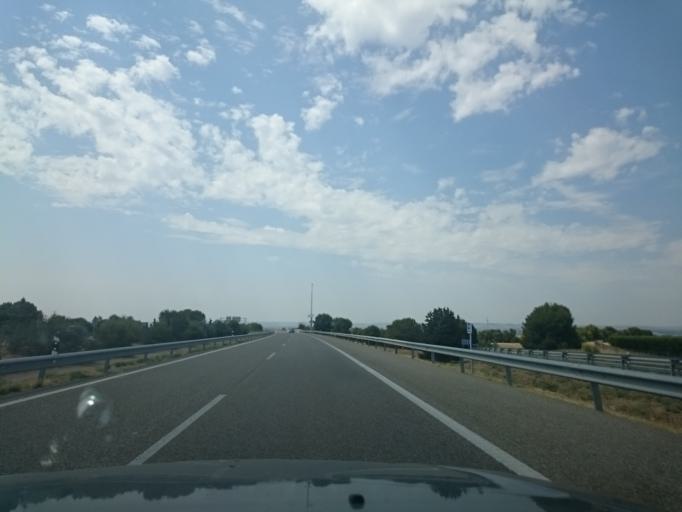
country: ES
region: Catalonia
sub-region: Provincia de Lleida
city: Alfes
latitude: 41.5502
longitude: 0.6223
